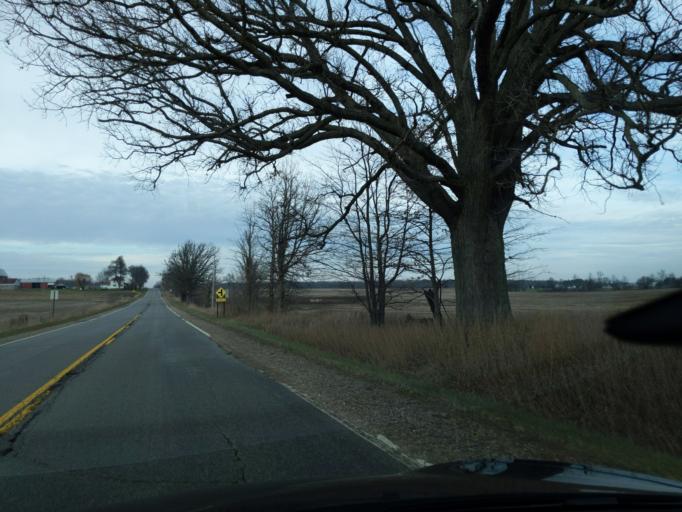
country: US
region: Michigan
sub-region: Ingham County
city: Williamston
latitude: 42.6521
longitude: -84.3637
